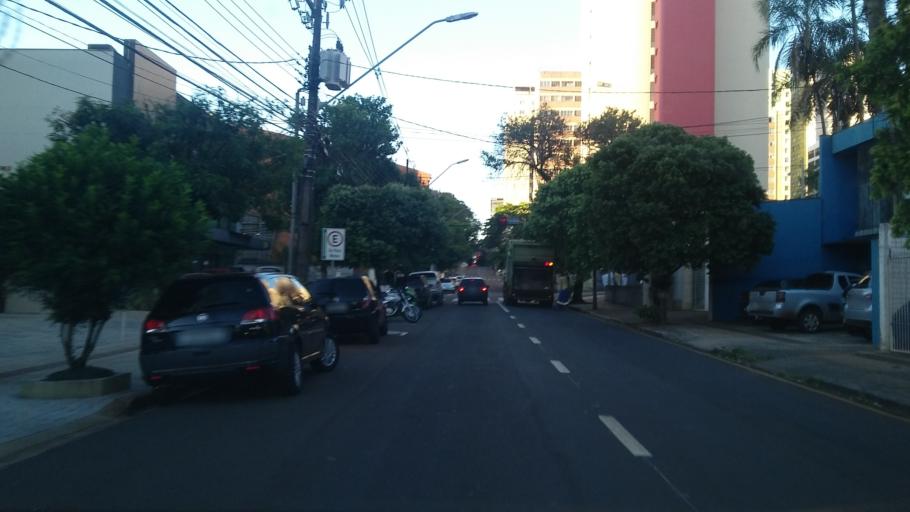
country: BR
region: Parana
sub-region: Londrina
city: Londrina
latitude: -23.3161
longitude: -51.1589
